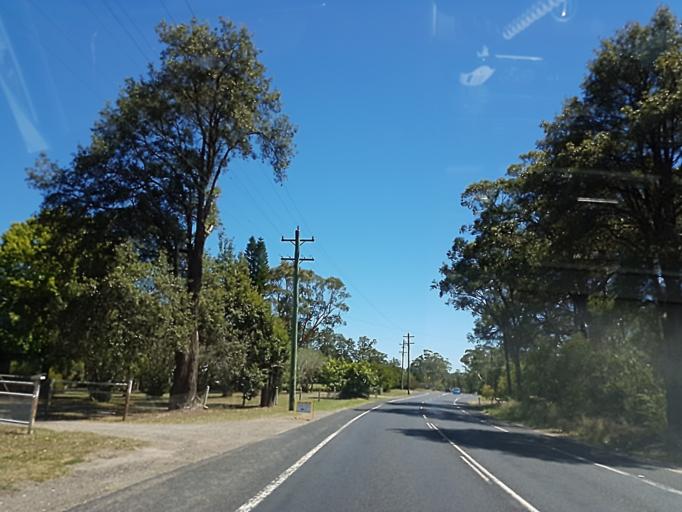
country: AU
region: New South Wales
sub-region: Hornsby Shire
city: Glenorie
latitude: -33.5974
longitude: 151.0063
